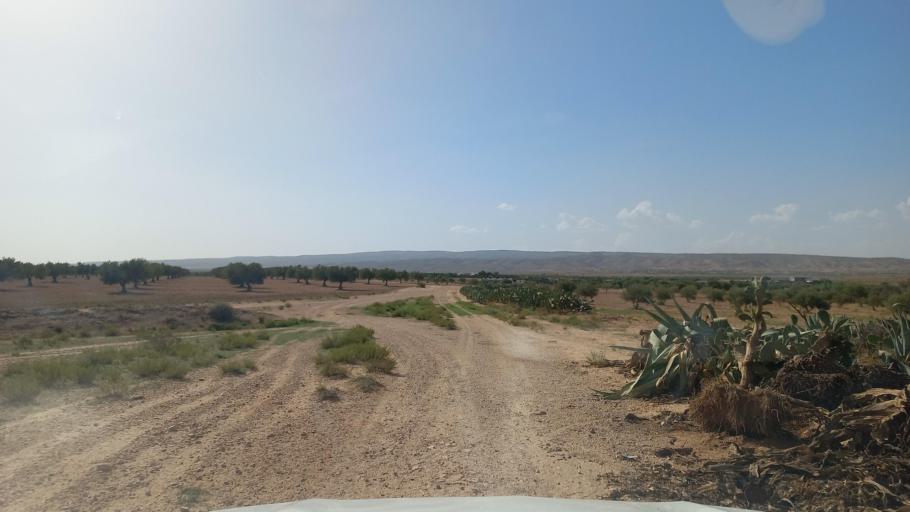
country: TN
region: Al Qasrayn
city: Kasserine
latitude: 35.3133
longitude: 9.0168
